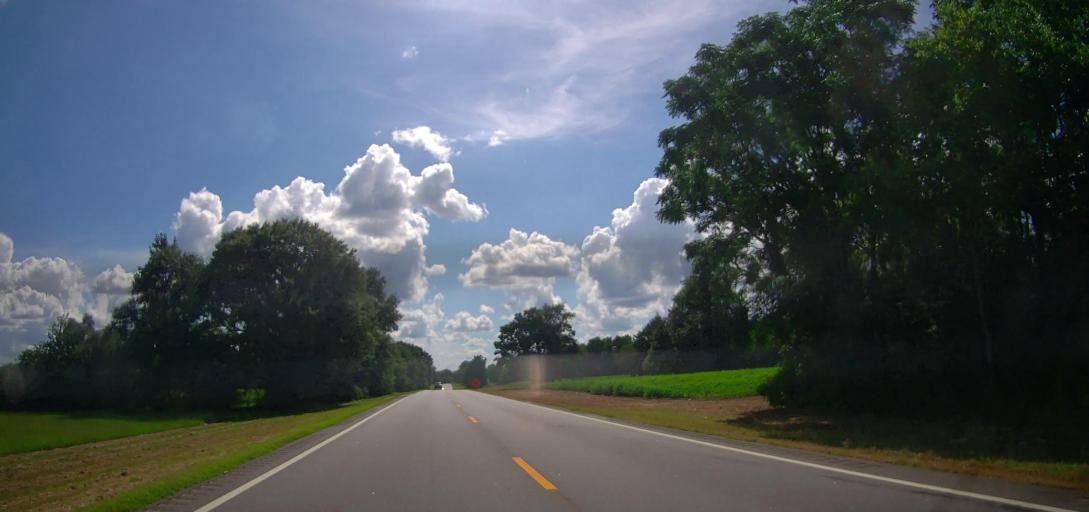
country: US
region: Alabama
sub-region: Lee County
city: Auburn
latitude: 32.4307
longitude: -85.4301
